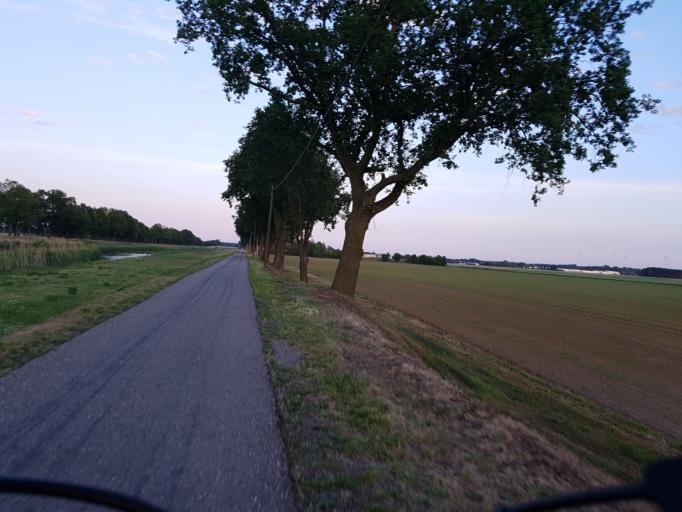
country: DE
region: Brandenburg
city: Falkenberg
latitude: 51.6134
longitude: 13.2988
